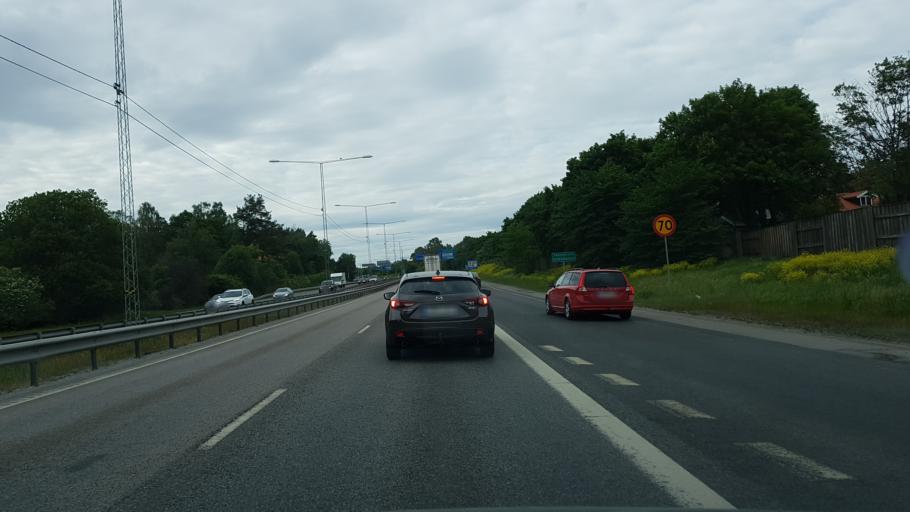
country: SE
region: Stockholm
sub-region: Stockholms Kommun
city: Arsta
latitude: 59.2534
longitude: 18.1000
